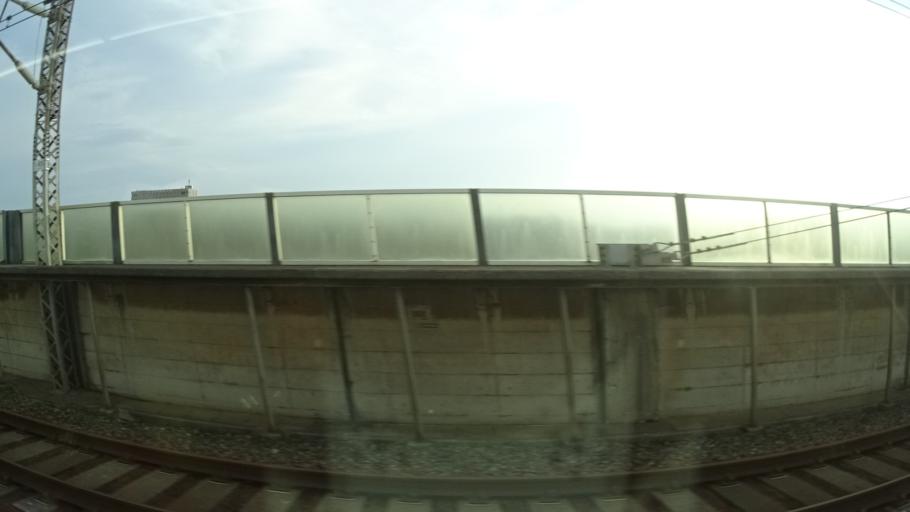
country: JP
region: Saitama
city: Ageoshimo
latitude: 35.9953
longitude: 139.6203
